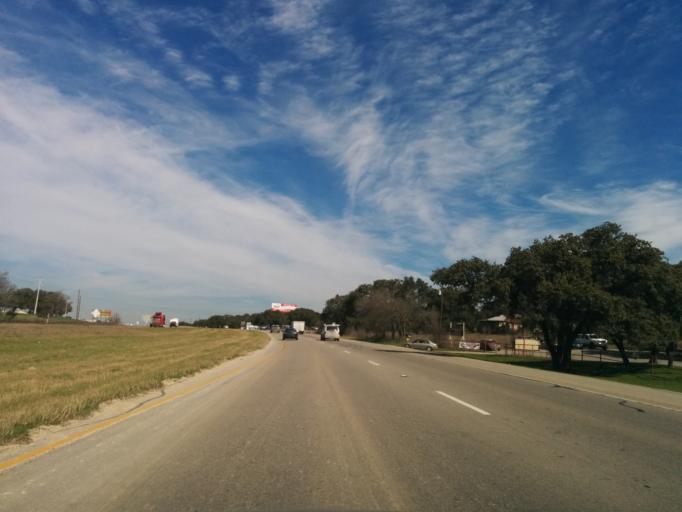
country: US
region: Texas
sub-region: Comal County
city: Bulverde
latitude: 29.8029
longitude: -98.4176
